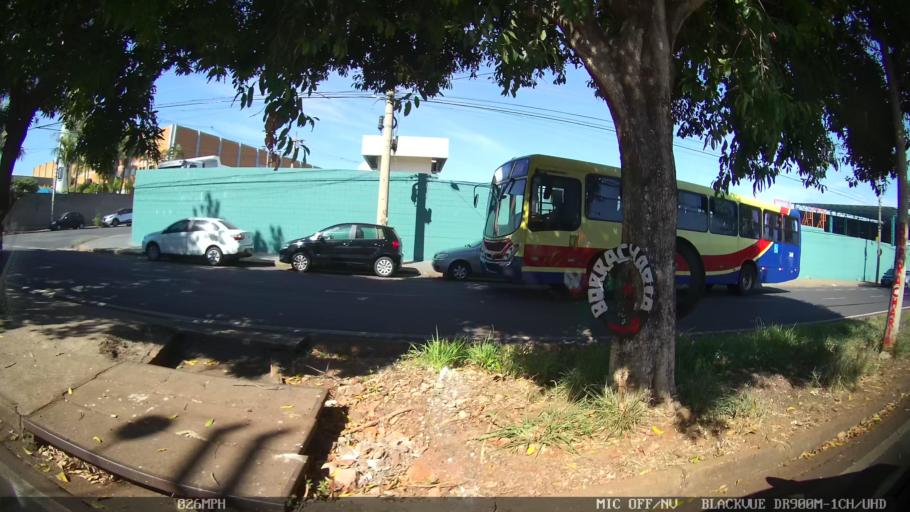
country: BR
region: Sao Paulo
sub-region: Sao Jose Do Rio Preto
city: Sao Jose do Rio Preto
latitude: -20.8126
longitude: -49.4279
